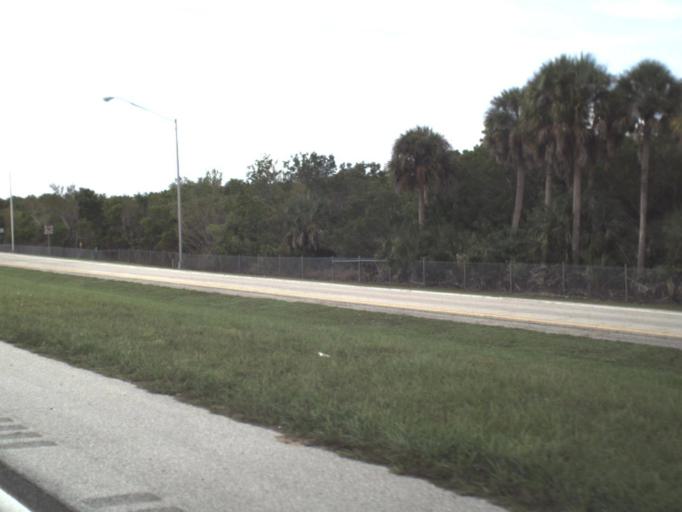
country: US
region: Florida
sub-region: Manatee County
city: Memphis
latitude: 27.5836
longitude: -82.6098
